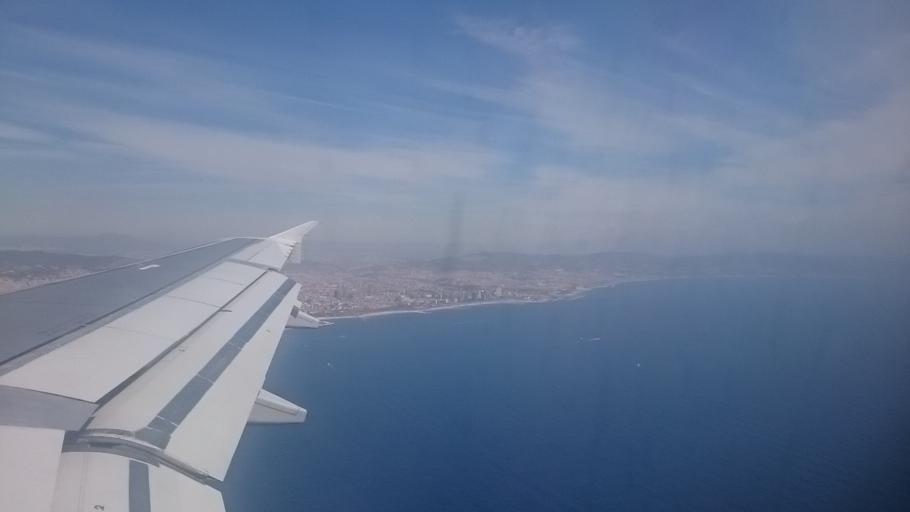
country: ES
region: Catalonia
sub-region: Provincia de Barcelona
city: Ciutat Vella
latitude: 41.3435
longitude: 2.2133
